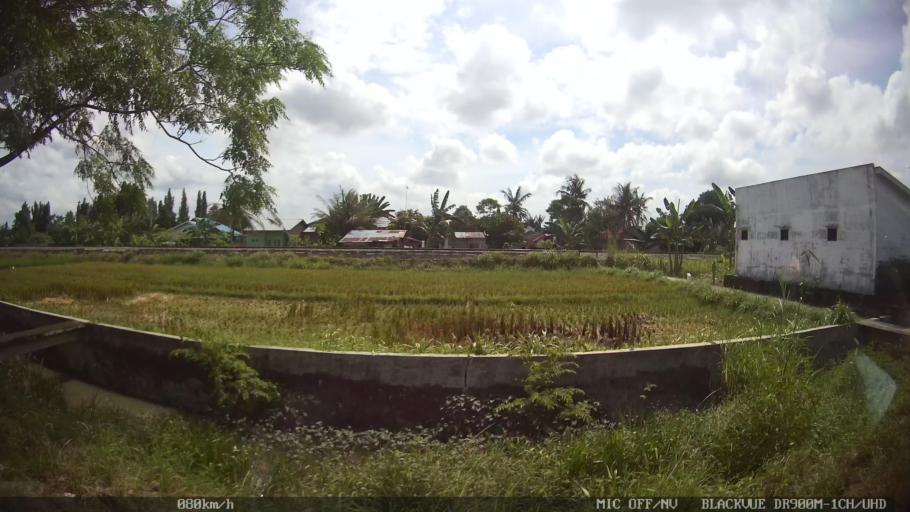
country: ID
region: North Sumatra
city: Percut
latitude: 3.5910
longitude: 98.8621
